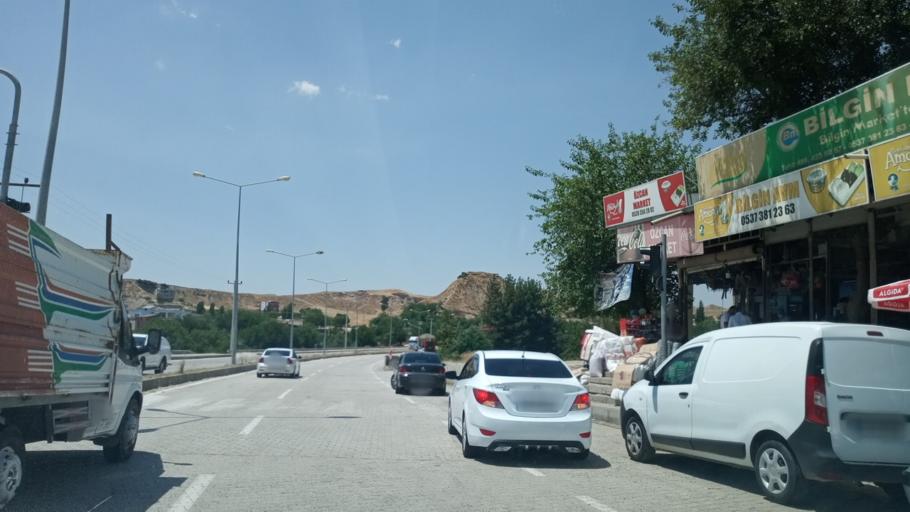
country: TR
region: Batman
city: Bekirhan
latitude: 38.1418
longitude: 41.2952
